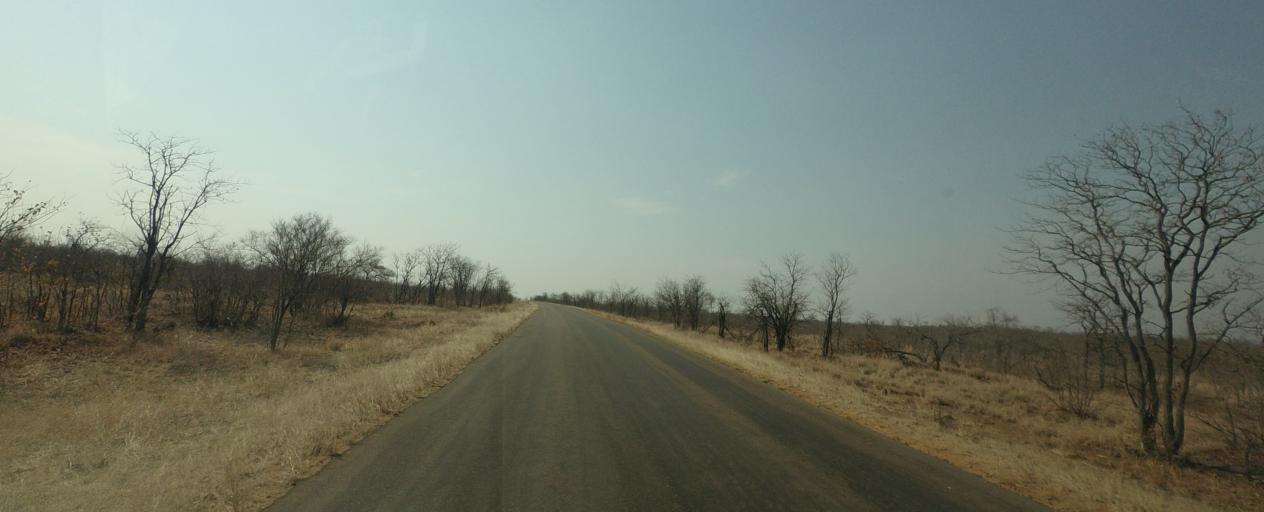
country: ZA
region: Limpopo
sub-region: Mopani District Municipality
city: Phalaborwa
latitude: -23.9437
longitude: 31.6140
